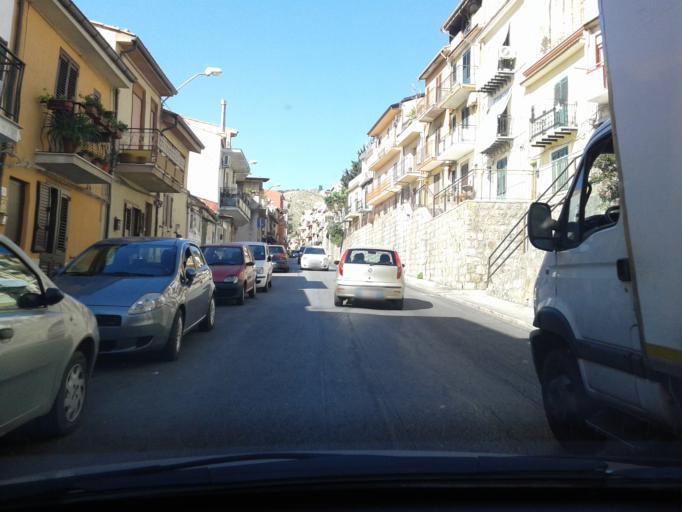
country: IT
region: Sicily
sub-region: Palermo
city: Pioppo
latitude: 38.0467
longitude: 13.2265
